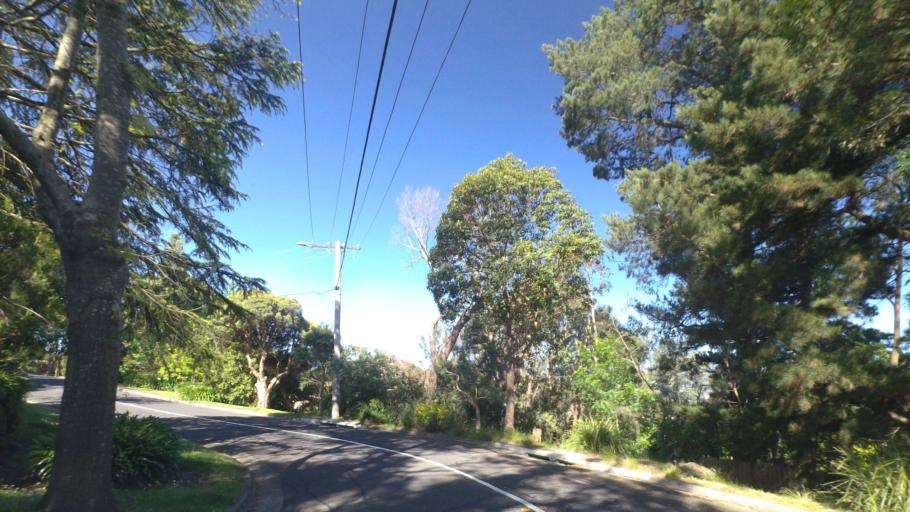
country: AU
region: Victoria
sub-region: Maroondah
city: Heathmont
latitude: -37.8296
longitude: 145.2521
